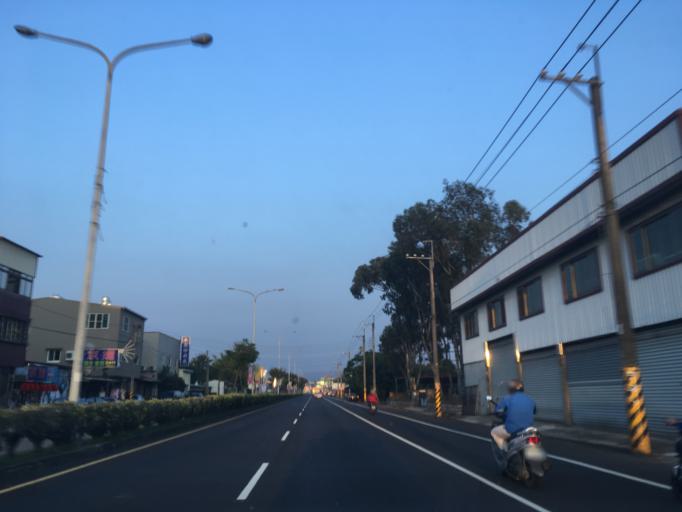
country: TW
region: Taiwan
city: Zhongxing New Village
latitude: 23.9881
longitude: 120.6728
